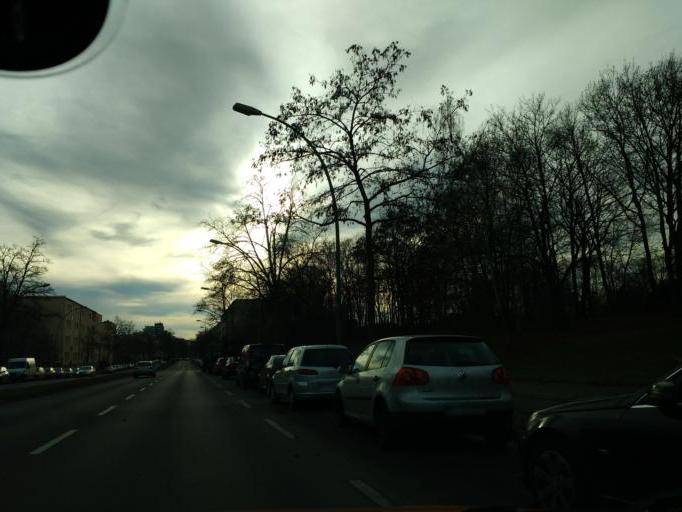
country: DE
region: Berlin
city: Schoneberg Bezirk
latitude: 52.4551
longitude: 13.3486
